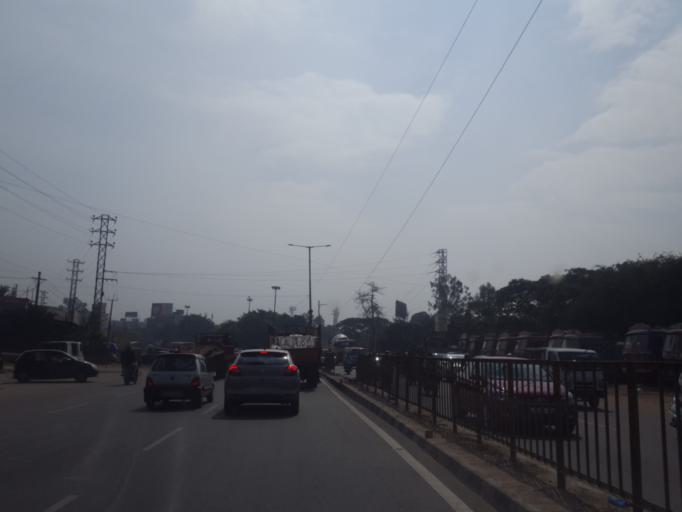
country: IN
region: Telangana
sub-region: Medak
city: Serilingampalle
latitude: 17.4971
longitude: 78.3146
